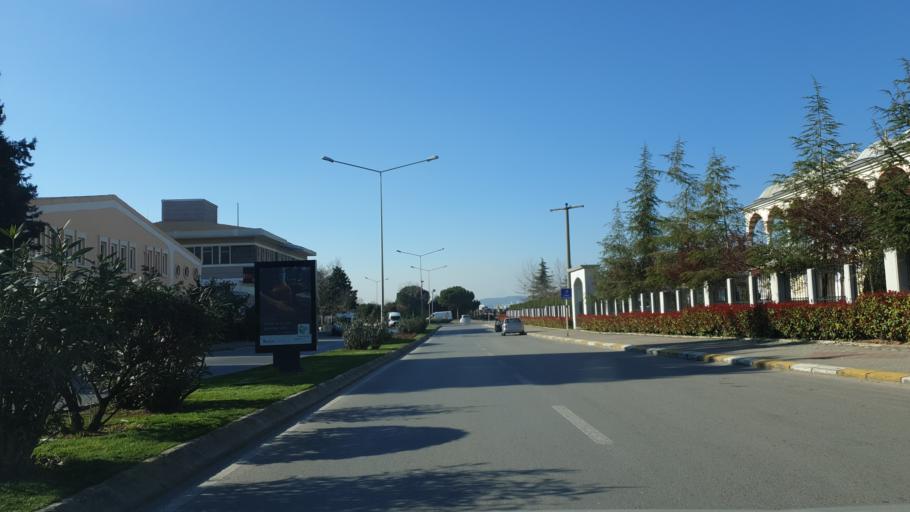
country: TR
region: Istanbul
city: Icmeler
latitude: 40.8801
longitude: 29.3503
